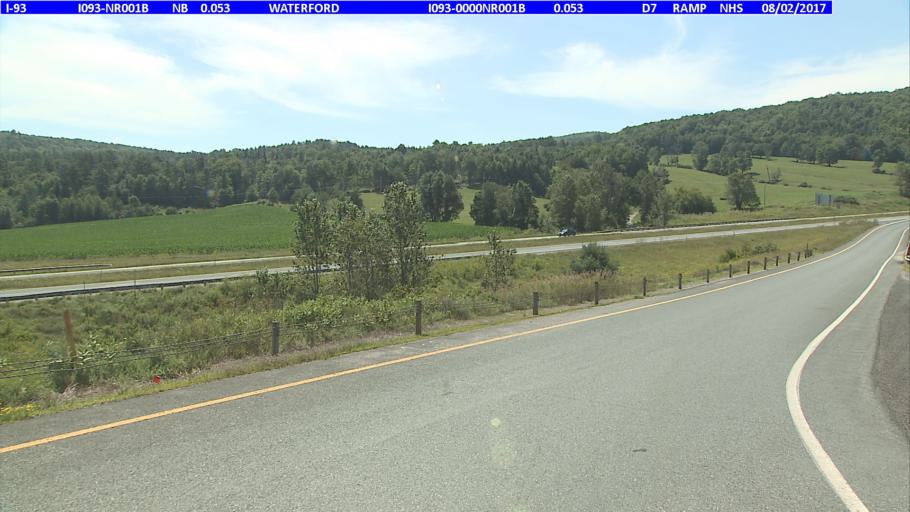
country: US
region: Vermont
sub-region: Caledonia County
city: St Johnsbury
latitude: 44.4257
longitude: -71.9567
